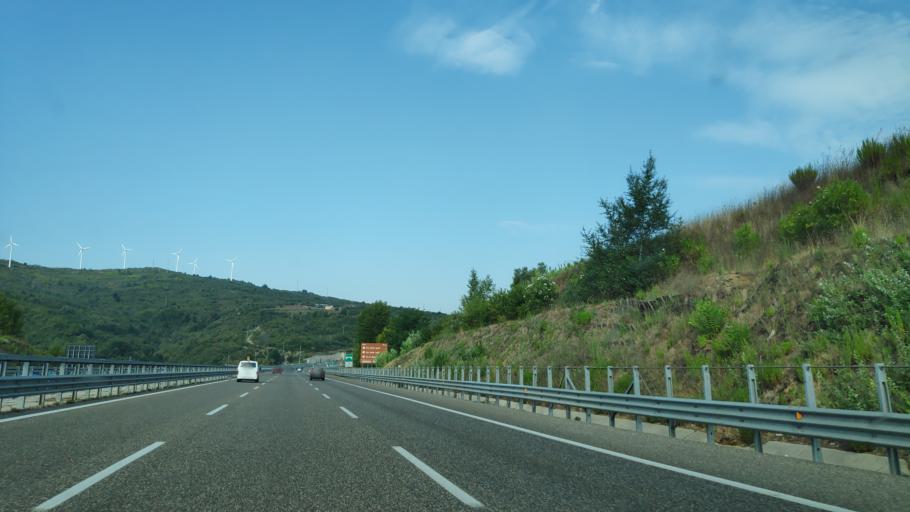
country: IT
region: Campania
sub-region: Provincia di Salerno
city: Contursi Terme
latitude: 40.6133
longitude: 15.2621
